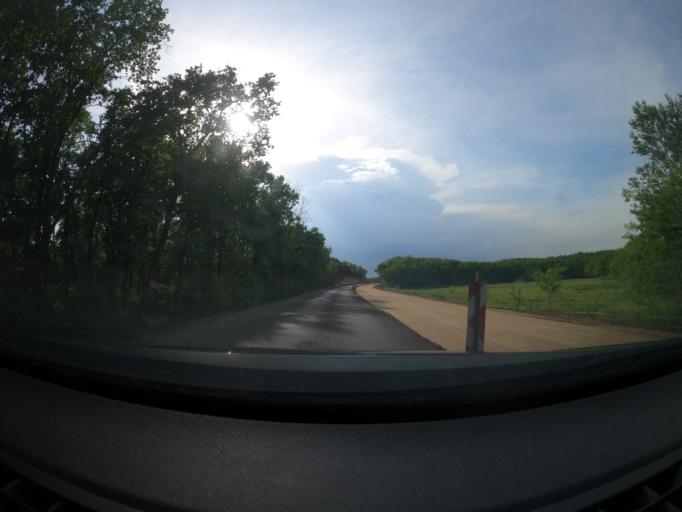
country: HU
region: Hajdu-Bihar
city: Vamospercs
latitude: 47.5239
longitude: 21.8727
